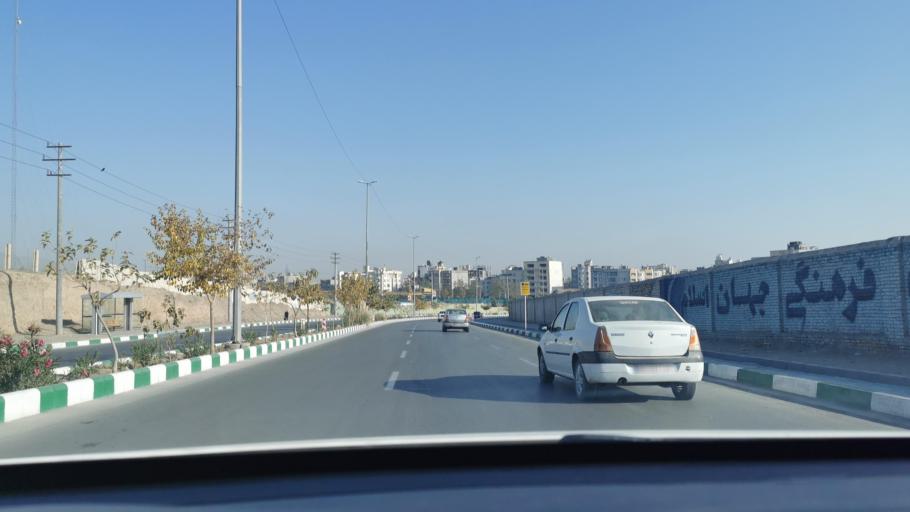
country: IR
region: Razavi Khorasan
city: Mashhad
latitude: 36.2804
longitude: 59.5417
